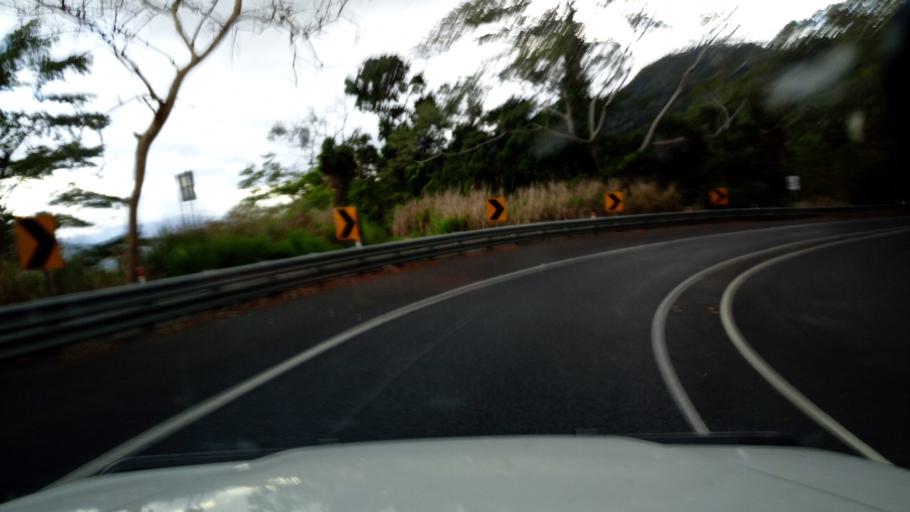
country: AU
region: Queensland
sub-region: Tablelands
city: Kuranda
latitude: -16.8380
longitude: 145.6726
